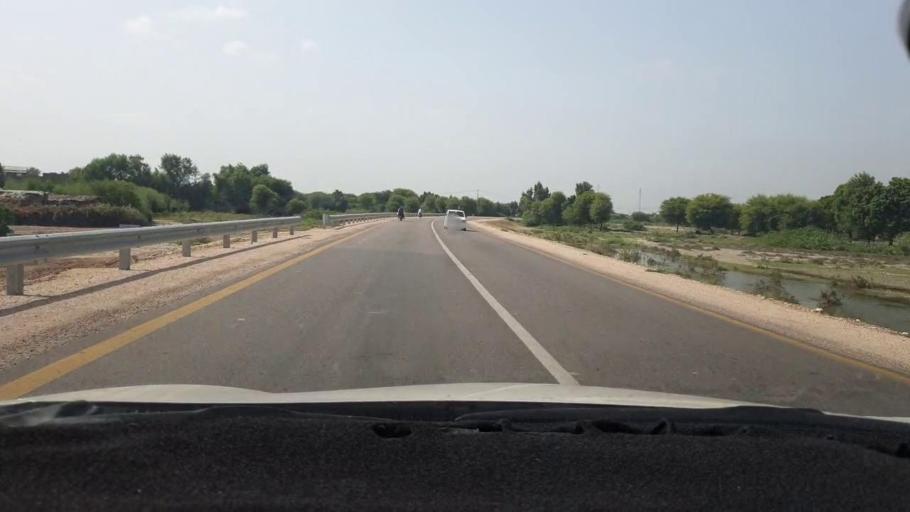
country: PK
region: Sindh
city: Mirpur Khas
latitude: 25.6258
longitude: 69.0909
